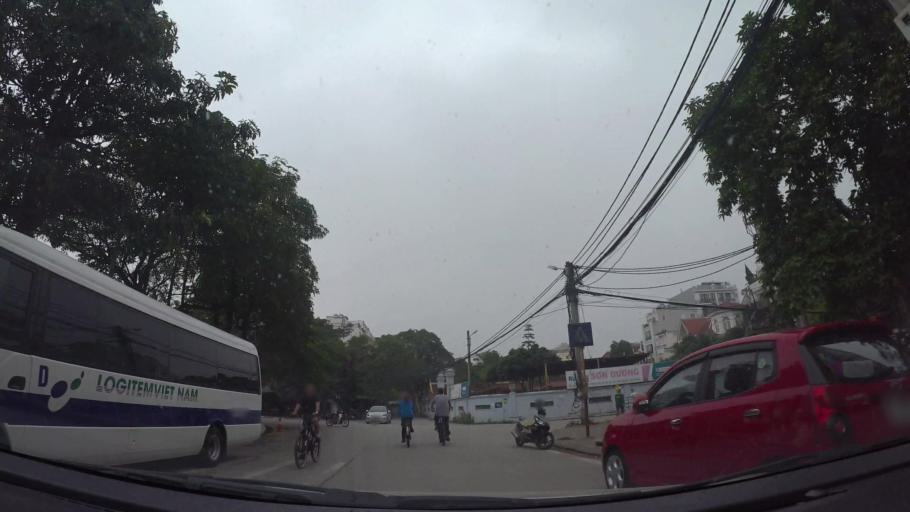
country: VN
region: Ha Noi
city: Tay Ho
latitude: 21.0663
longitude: 105.8233
